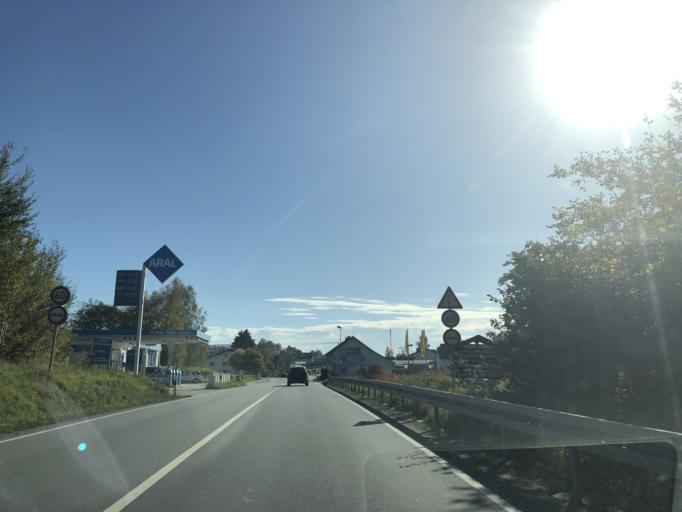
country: DE
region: Bavaria
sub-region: Lower Bavaria
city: Ruhmannsfelden
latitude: 48.9853
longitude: 12.9808
